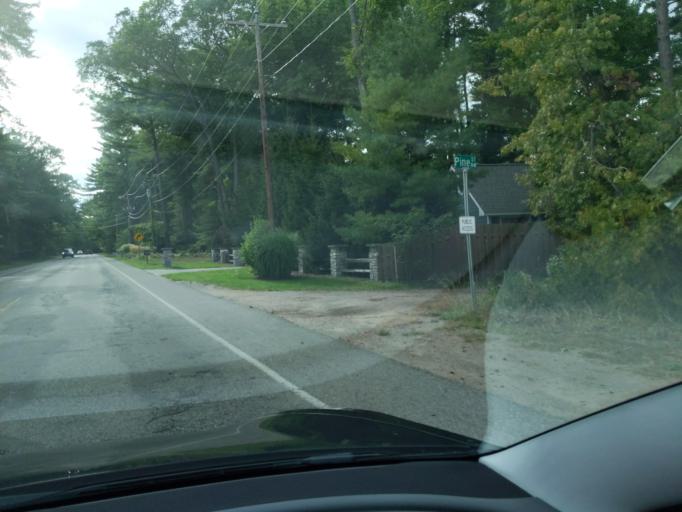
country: US
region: Michigan
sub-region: Kalkaska County
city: Rapid City
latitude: 44.8528
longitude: -85.3134
